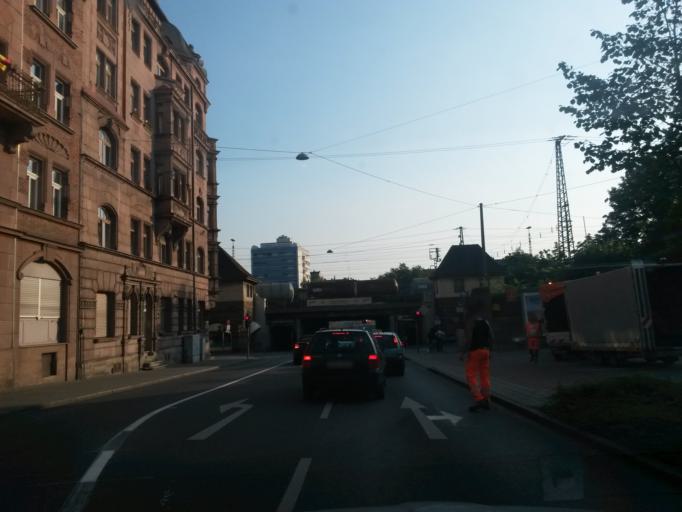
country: DE
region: Bavaria
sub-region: Regierungsbezirk Mittelfranken
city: Furth
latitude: 49.4665
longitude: 11.0004
